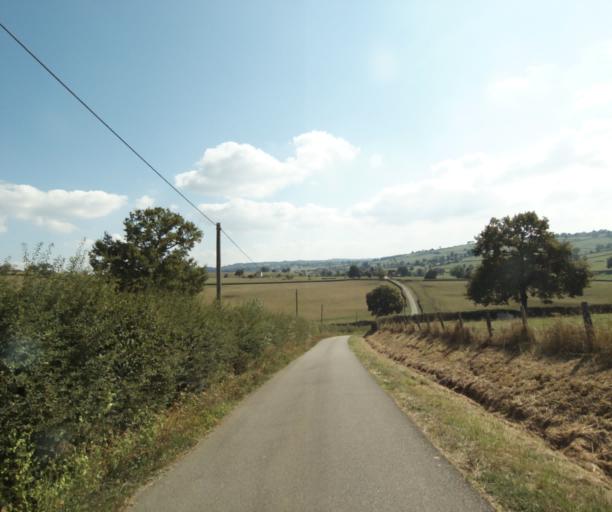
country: FR
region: Bourgogne
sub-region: Departement de Saone-et-Loire
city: Charolles
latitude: 46.3777
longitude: 4.2223
